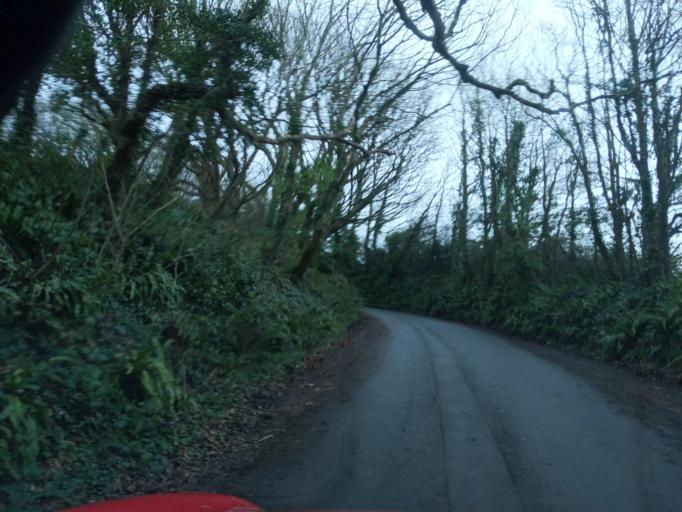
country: GB
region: England
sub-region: Devon
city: Wembury
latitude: 50.3257
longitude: -4.0781
